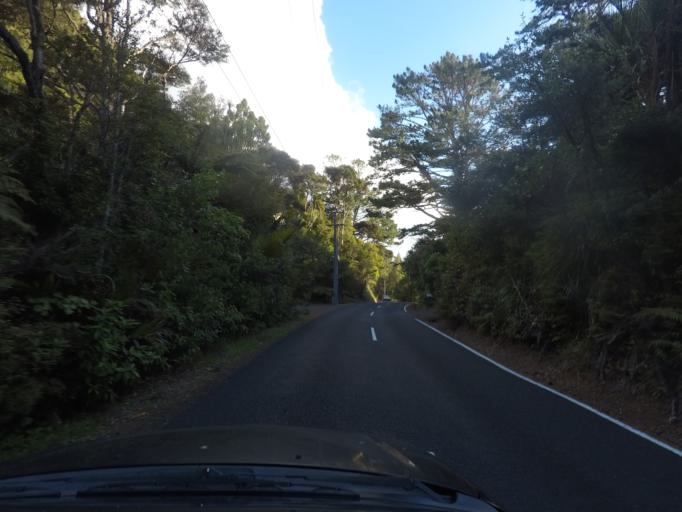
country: NZ
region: Auckland
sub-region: Auckland
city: Titirangi
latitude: -36.9354
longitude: 174.6186
